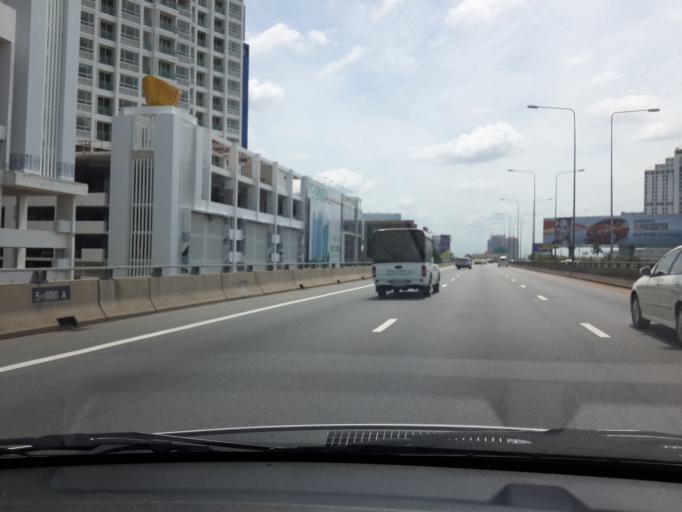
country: TH
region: Bangkok
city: Huai Khwang
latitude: 13.7532
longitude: 100.5748
